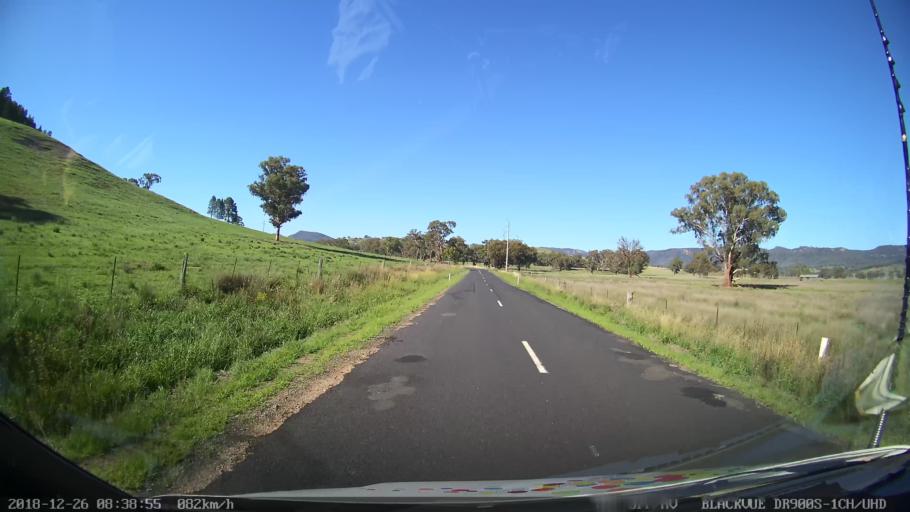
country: AU
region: New South Wales
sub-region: Upper Hunter Shire
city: Merriwa
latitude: -32.4477
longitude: 150.0783
